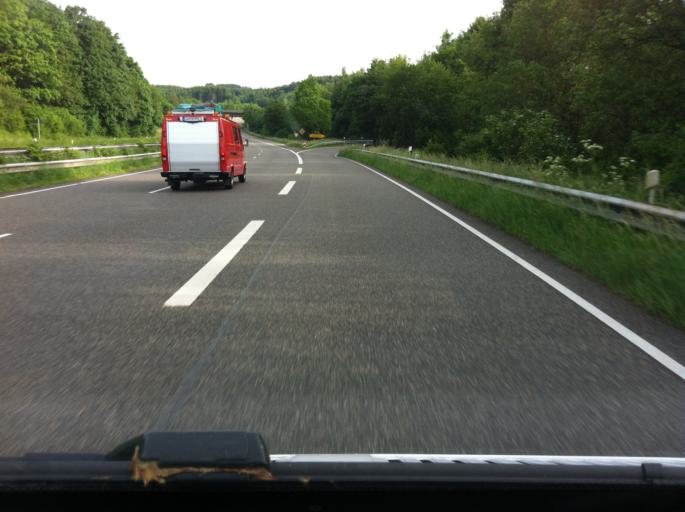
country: DE
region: Rheinland-Pfalz
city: Kerschenbach
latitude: 50.3653
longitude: 6.5096
